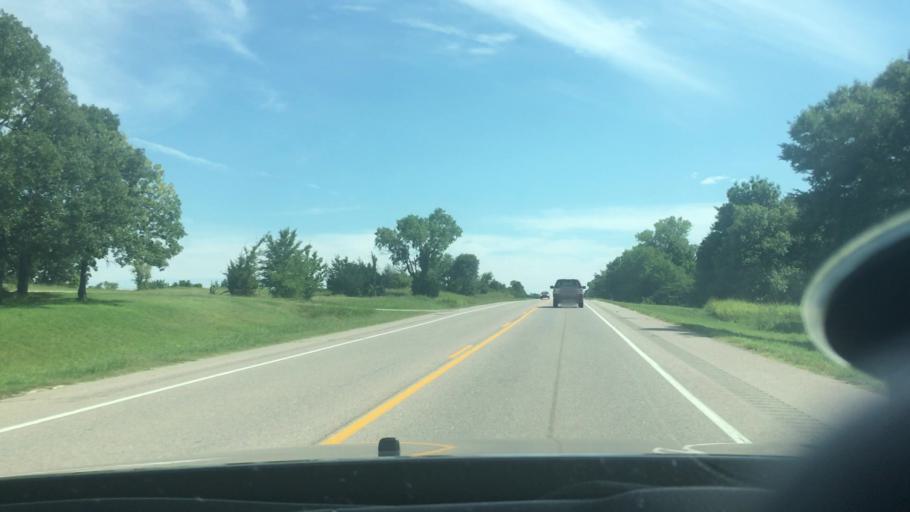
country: US
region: Oklahoma
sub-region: Seminole County
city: Konawa
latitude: 35.0226
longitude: -96.6783
